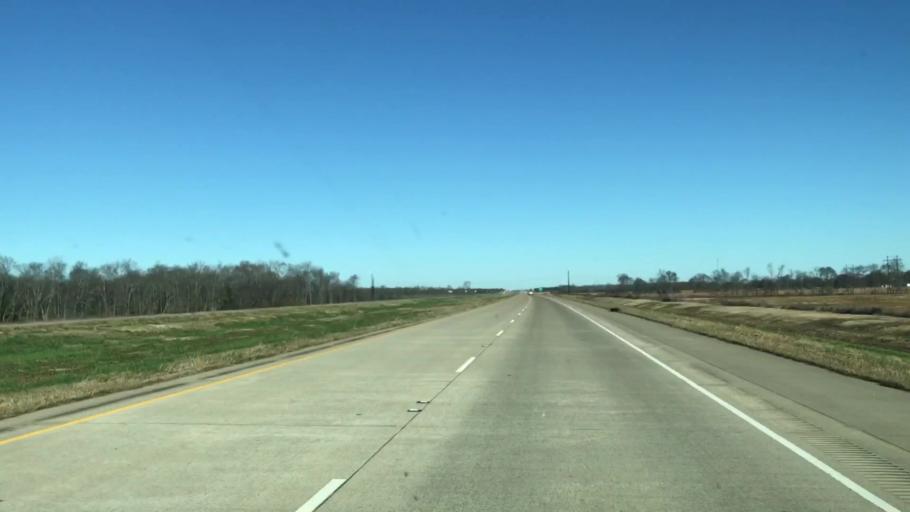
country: US
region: Louisiana
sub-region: Caddo Parish
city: Blanchard
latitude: 32.6571
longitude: -93.8427
